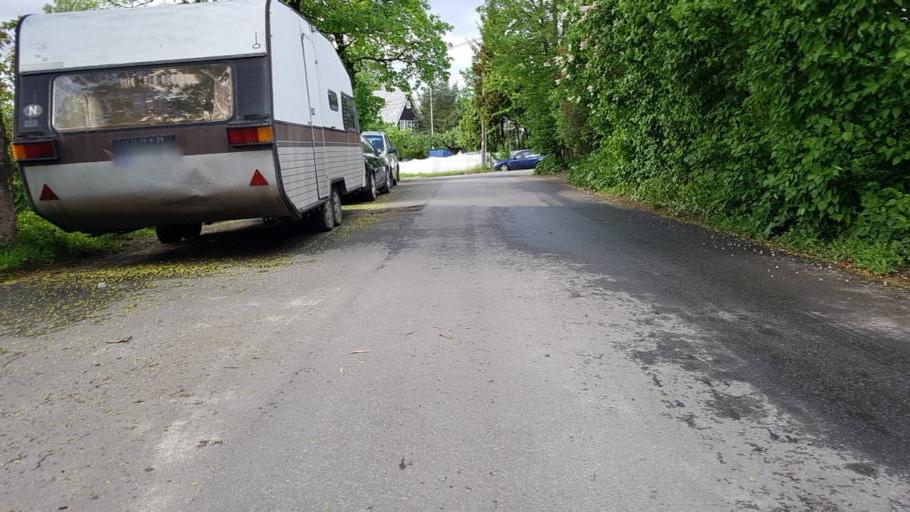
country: NO
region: Oslo
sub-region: Oslo
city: Oslo
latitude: 59.9432
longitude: 10.7884
